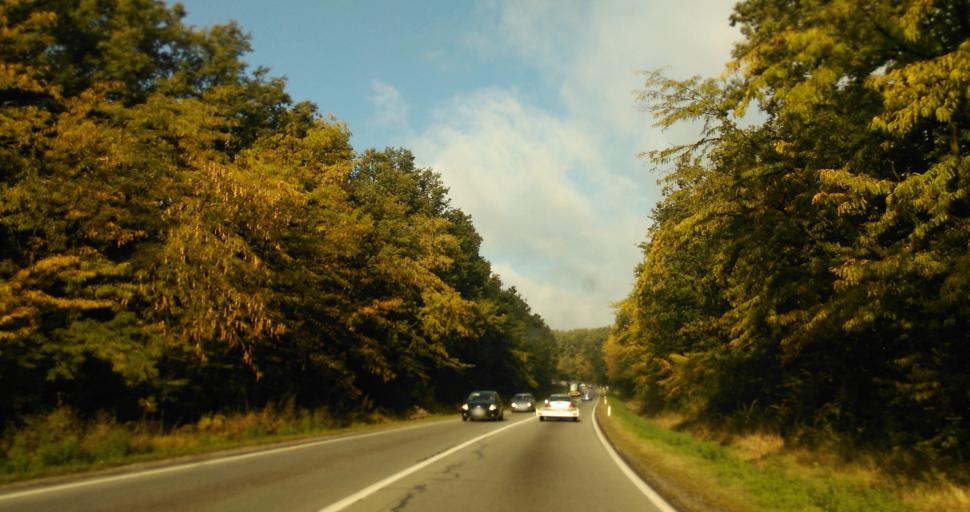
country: RS
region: Central Serbia
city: Sremcica
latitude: 44.6329
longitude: 20.3948
